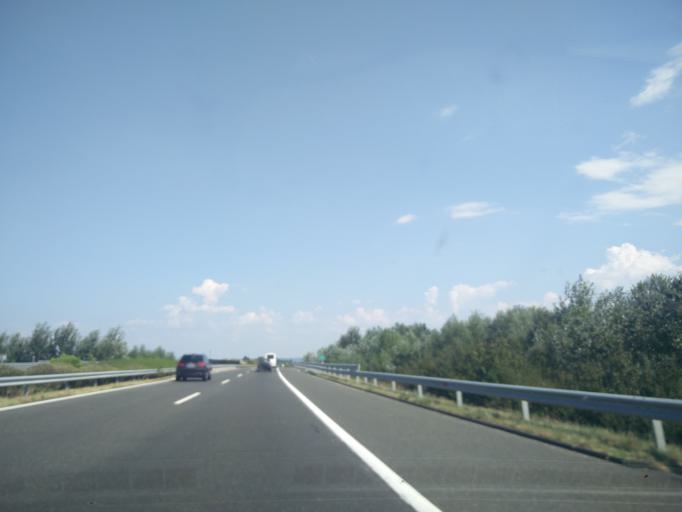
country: HU
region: Somogy
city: Balatonfenyves
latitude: 46.7028
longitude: 17.4827
